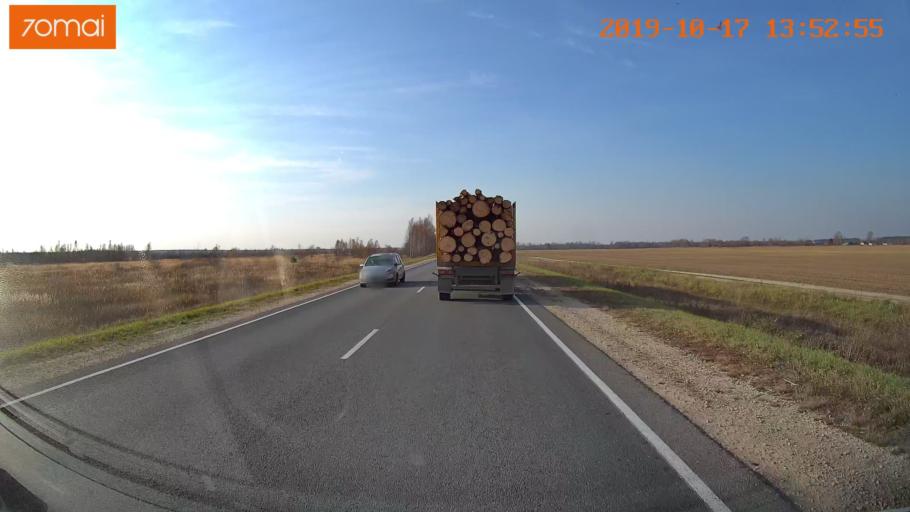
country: RU
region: Rjazan
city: Spas-Klepiki
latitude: 55.1414
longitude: 40.3511
